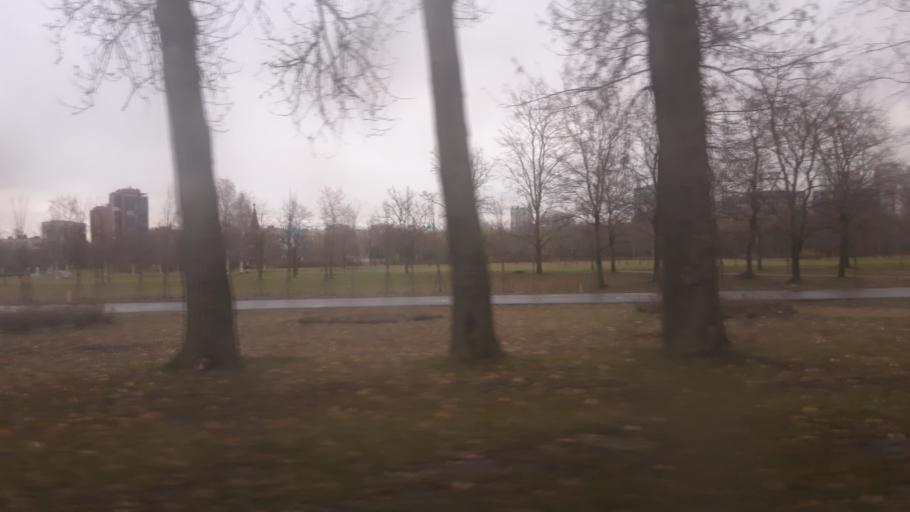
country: RU
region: St.-Petersburg
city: Kupchino
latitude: 59.8354
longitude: 30.3227
